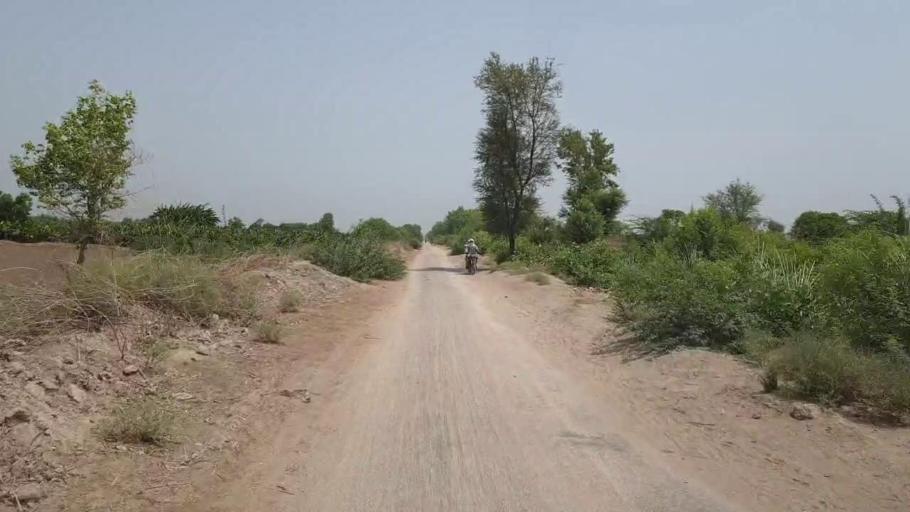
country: PK
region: Sindh
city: Nawabshah
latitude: 26.3044
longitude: 68.3037
